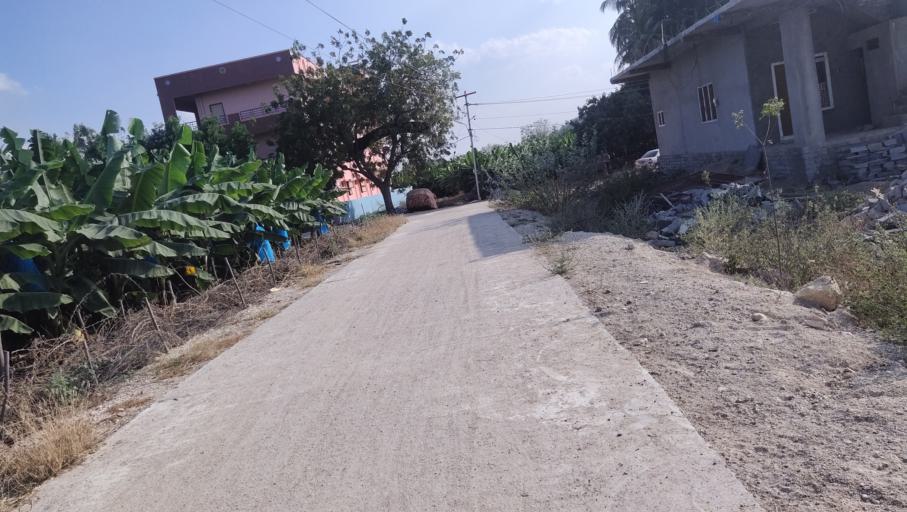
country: IN
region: Andhra Pradesh
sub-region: Anantapur
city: Tadpatri
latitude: 14.9320
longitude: 77.8660
